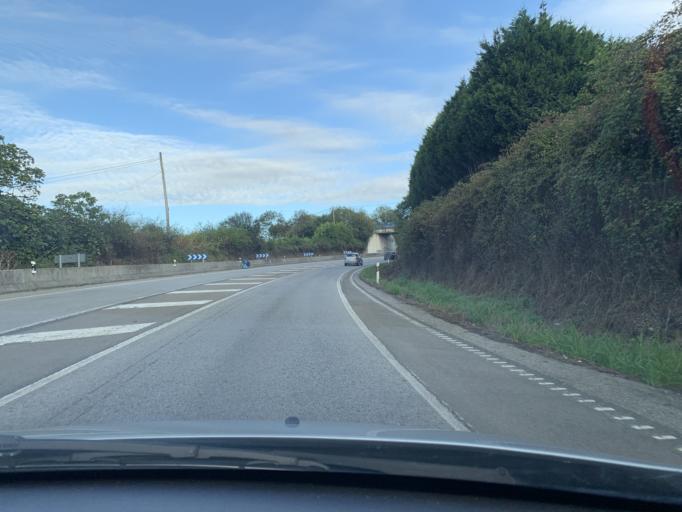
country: ES
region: Galicia
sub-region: Provincia de Lugo
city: Foz
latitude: 43.5546
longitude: -7.2674
